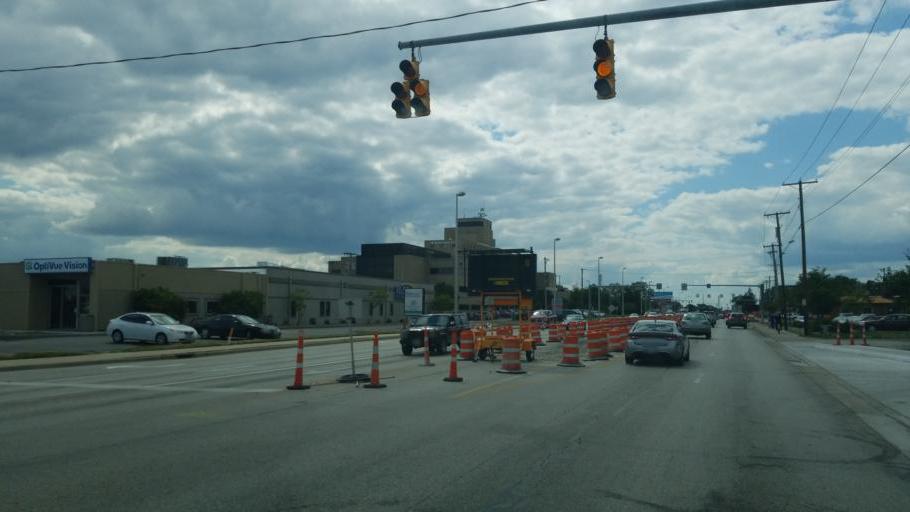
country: US
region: Ohio
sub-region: Lucas County
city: Oregon
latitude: 41.6368
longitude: -83.4824
